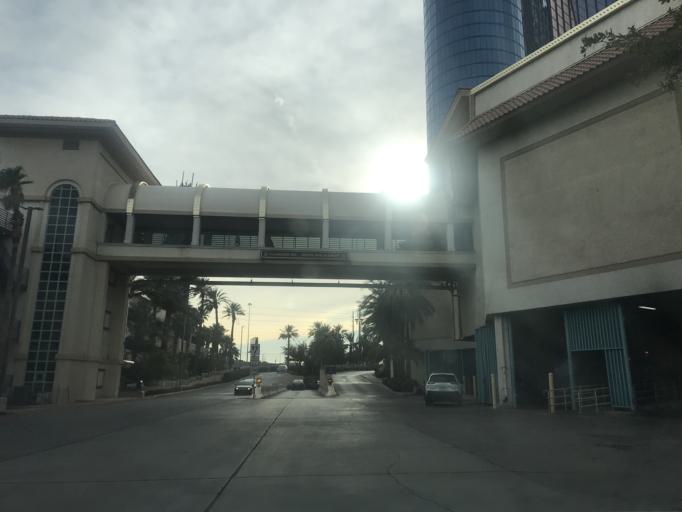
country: US
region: Nevada
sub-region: Clark County
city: Paradise
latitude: 36.1170
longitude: -115.1851
